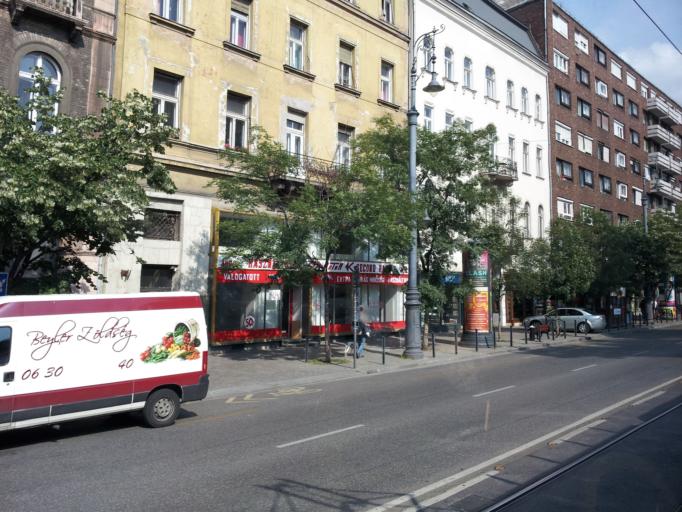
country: HU
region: Budapest
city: Budapest IX. keruelet
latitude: 47.4904
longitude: 19.0614
